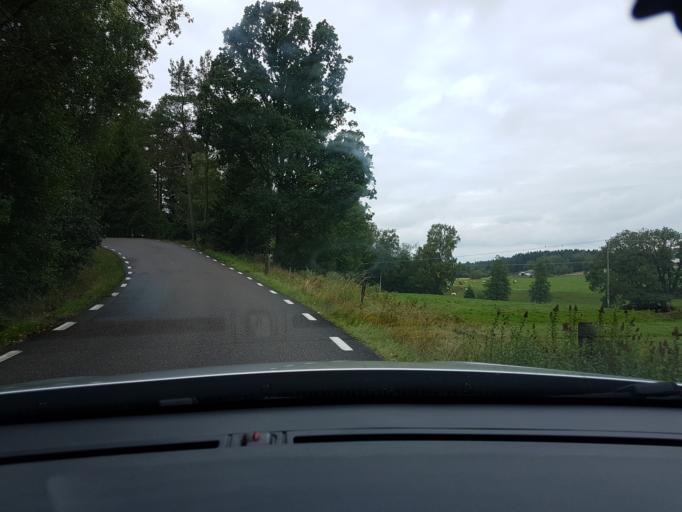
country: SE
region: Vaestra Goetaland
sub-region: Ale Kommun
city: Alvangen
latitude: 57.9089
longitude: 12.1616
